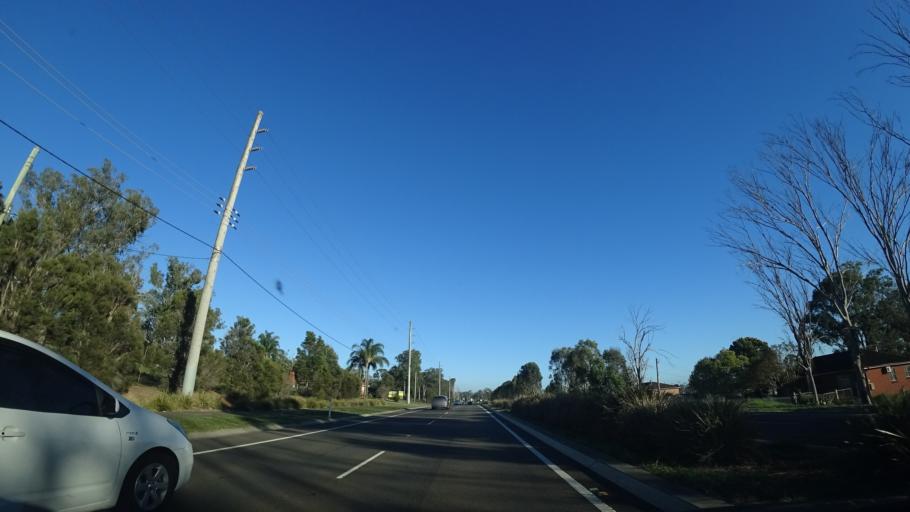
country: AU
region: New South Wales
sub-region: Blacktown
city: Riverstone
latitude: -33.6422
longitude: 150.8541
